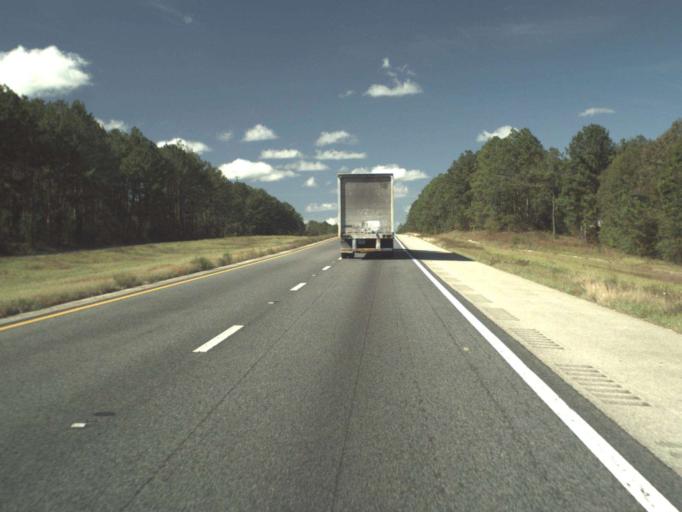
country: US
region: Florida
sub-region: Washington County
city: Chipley
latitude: 30.7465
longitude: -85.5178
